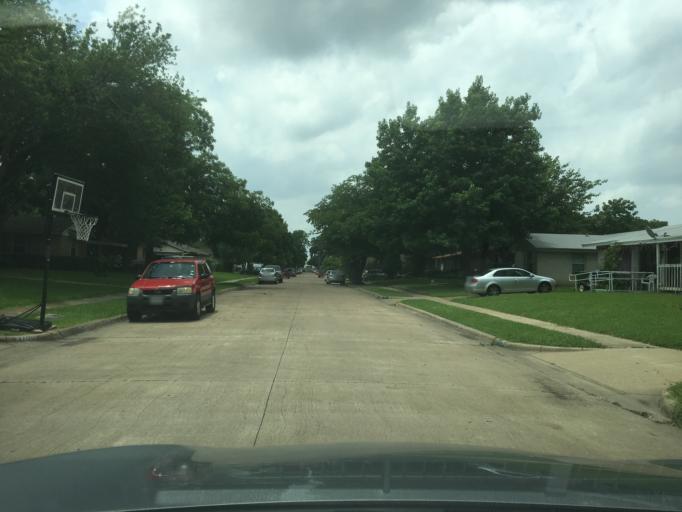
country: US
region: Texas
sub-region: Dallas County
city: Garland
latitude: 32.9183
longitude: -96.6749
